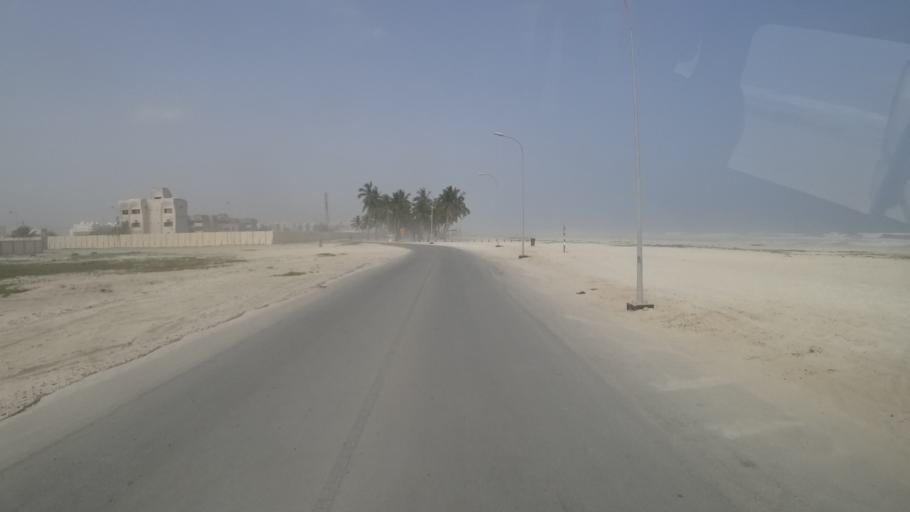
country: OM
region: Zufar
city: Salalah
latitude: 17.0102
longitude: 54.1668
